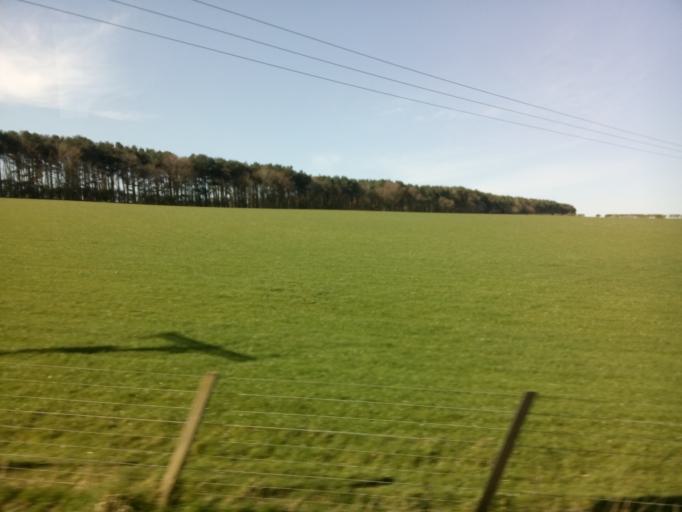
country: GB
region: Scotland
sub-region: The Scottish Borders
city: Chirnside
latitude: 55.8364
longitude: -2.1594
